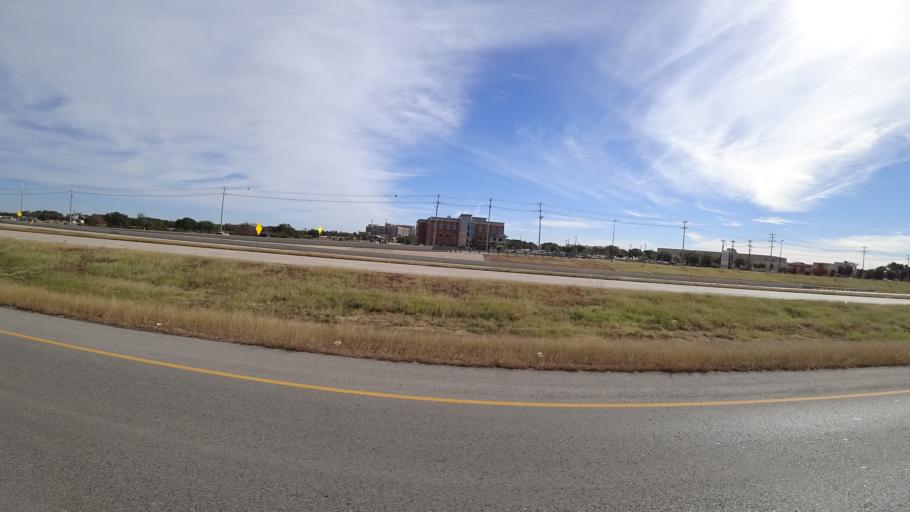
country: US
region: Texas
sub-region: Williamson County
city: Cedar Park
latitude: 30.5330
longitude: -97.8175
